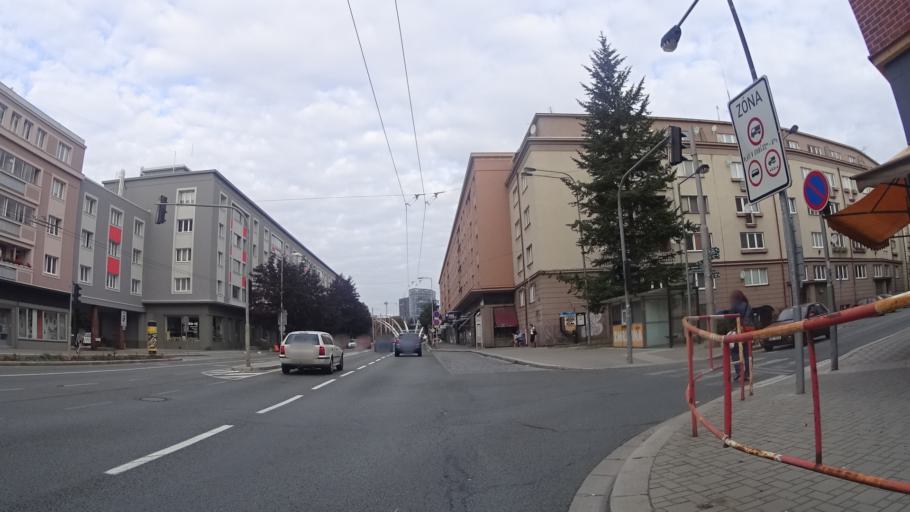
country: CZ
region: Kralovehradecky
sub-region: Okres Hradec Kralove
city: Hradec Kralove
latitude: 50.2115
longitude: 15.8171
